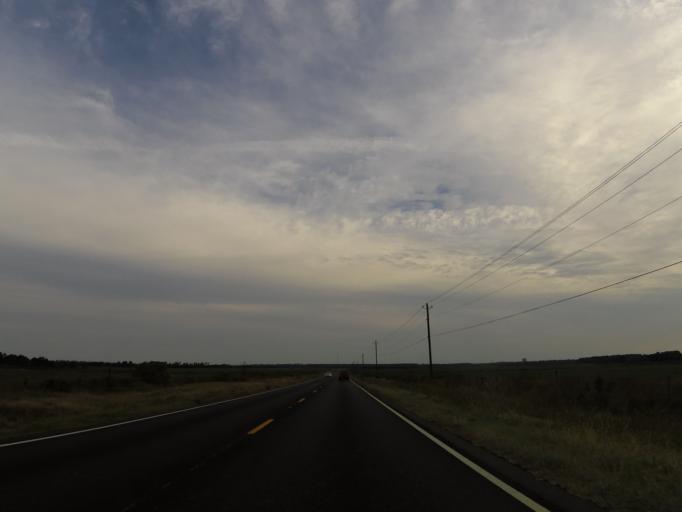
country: US
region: Alabama
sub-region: Escambia County
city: Atmore
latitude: 31.1474
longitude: -87.4636
